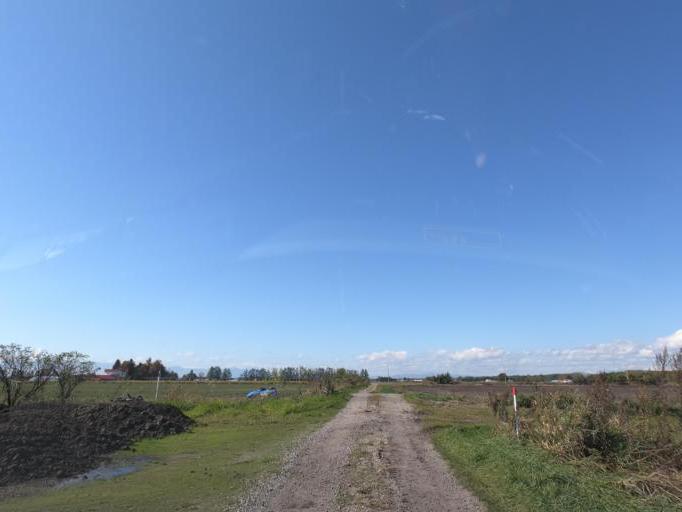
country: JP
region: Hokkaido
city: Otofuke
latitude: 43.0714
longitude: 143.2615
